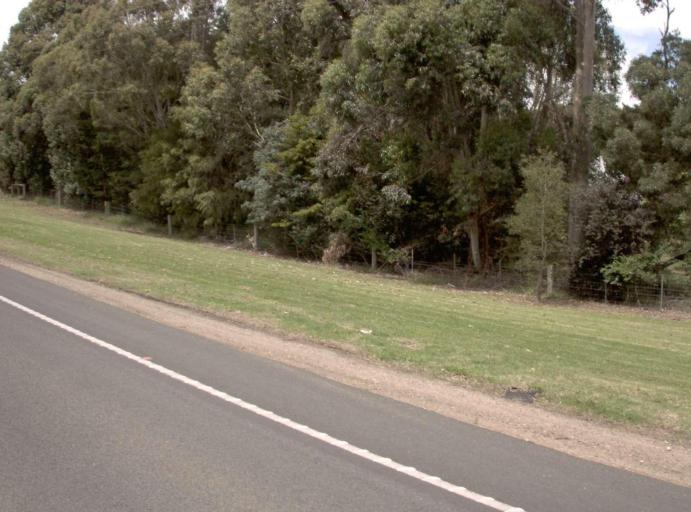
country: AU
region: Victoria
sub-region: Wellington
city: Sale
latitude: -38.0792
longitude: 147.0492
